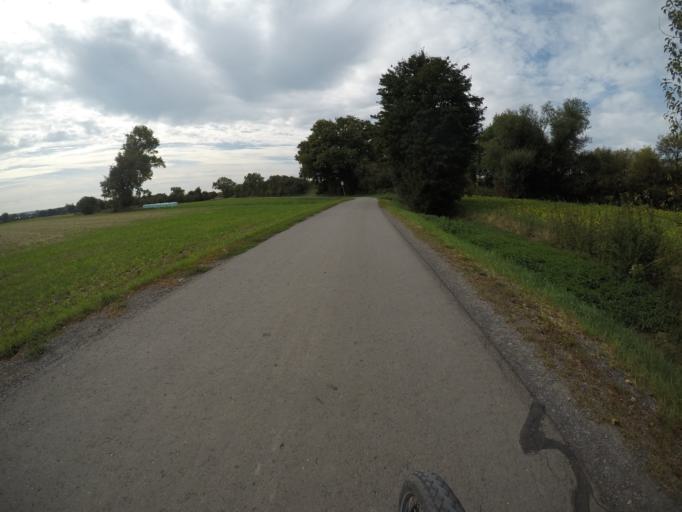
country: DE
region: Baden-Wuerttemberg
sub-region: Karlsruhe Region
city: Kronau
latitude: 49.2338
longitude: 8.6314
